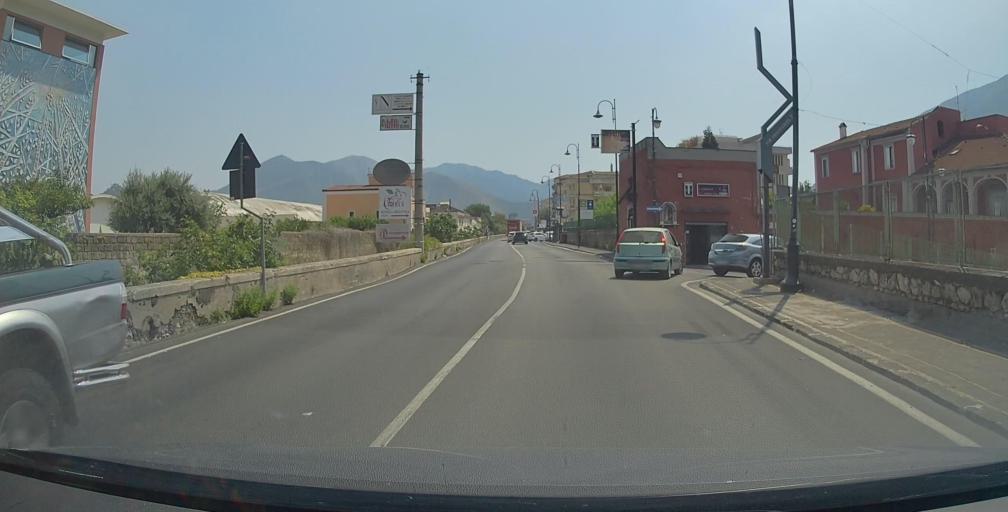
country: IT
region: Campania
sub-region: Provincia di Salerno
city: Nocera Inferiore
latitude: 40.7410
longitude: 14.6509
